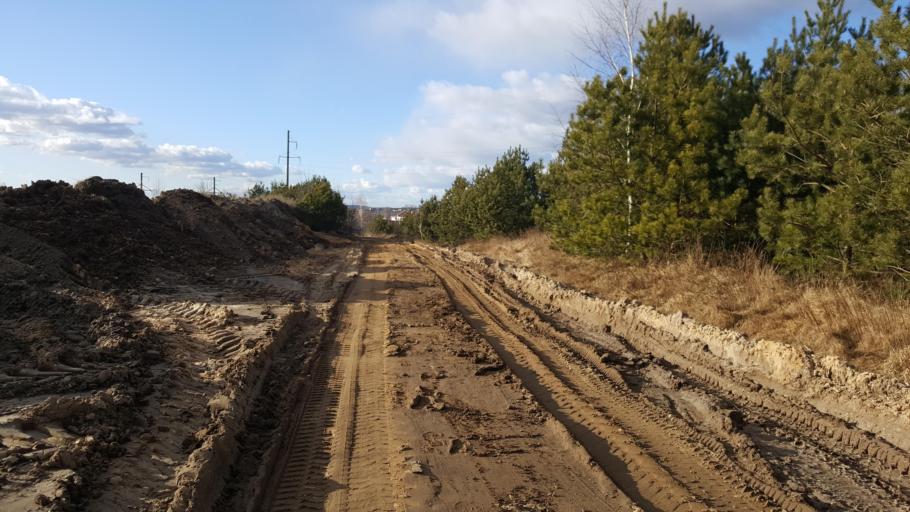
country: BY
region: Brest
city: Kamyanyets
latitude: 52.3886
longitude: 23.8347
